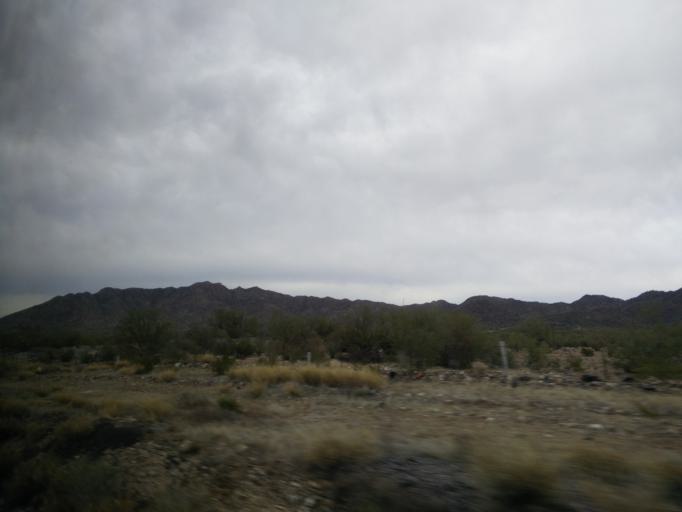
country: MX
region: Sonora
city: Hermosillo
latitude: 28.9513
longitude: -110.9624
